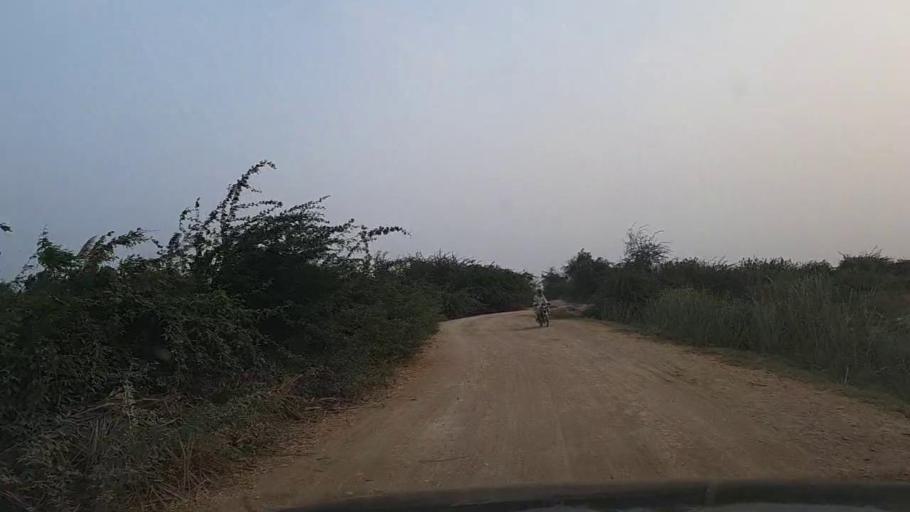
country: PK
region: Sindh
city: Gharo
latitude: 24.7399
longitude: 67.6941
